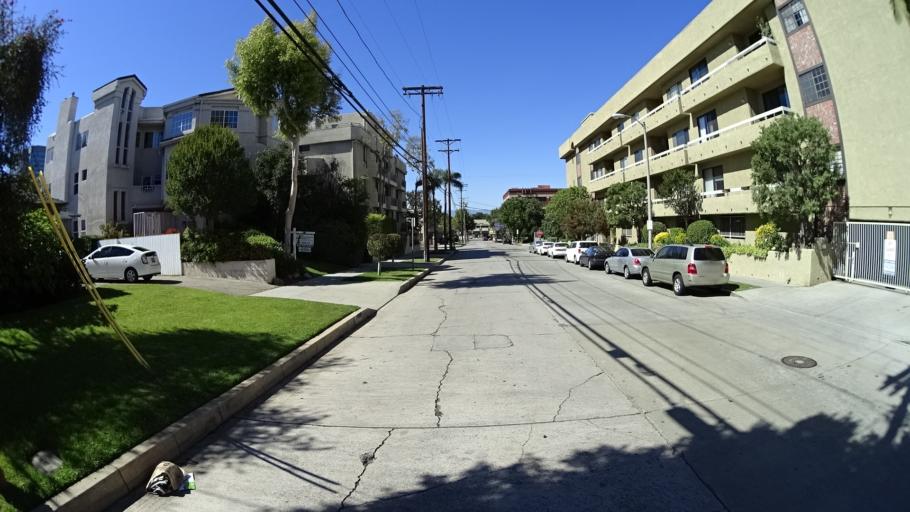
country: US
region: California
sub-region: Los Angeles County
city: Sherman Oaks
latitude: 34.1513
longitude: -118.4621
